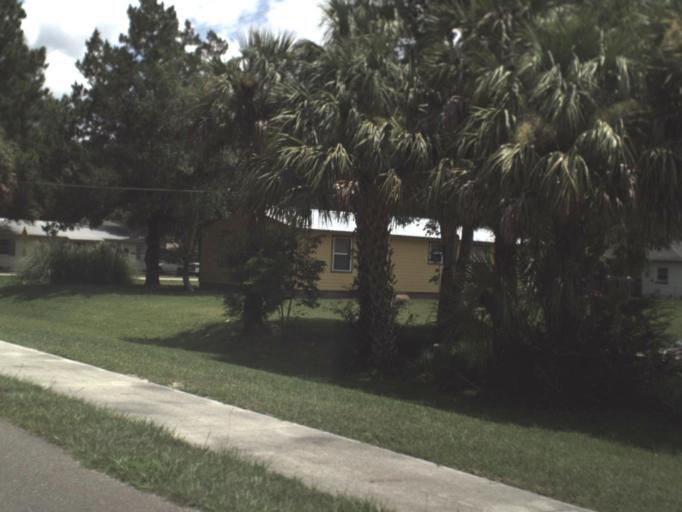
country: US
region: Florida
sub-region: Union County
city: Lake Butler
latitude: 30.0108
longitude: -82.3444
